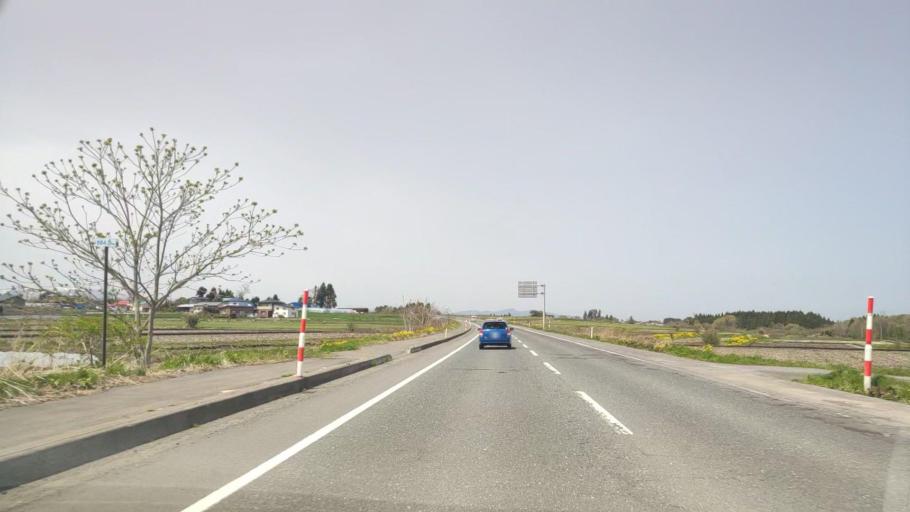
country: JP
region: Aomori
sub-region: Misawa Shi
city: Inuotose
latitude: 40.6347
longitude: 141.2444
